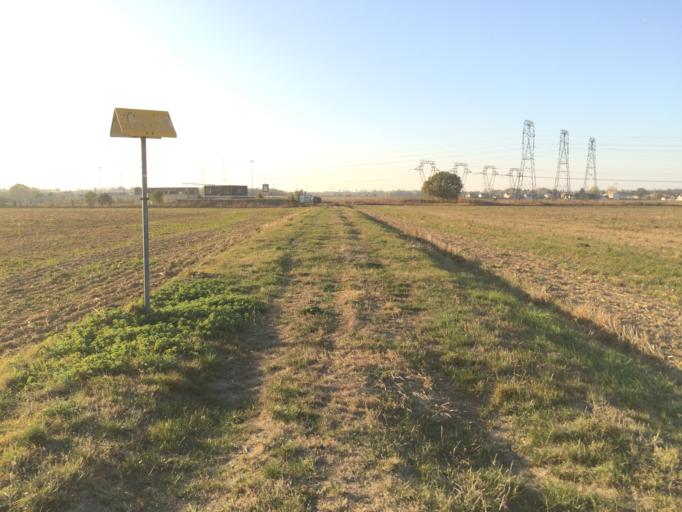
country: FR
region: Ile-de-France
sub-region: Departement de l'Essonne
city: Nozay
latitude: 48.6645
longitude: 2.2208
